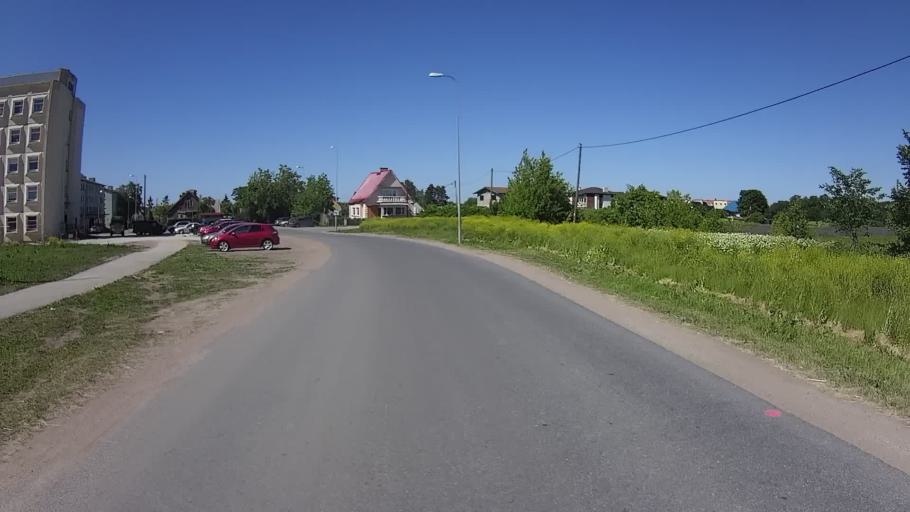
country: EE
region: Ida-Virumaa
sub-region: Kohtla-Jaerve linn
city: Kohtla-Jarve
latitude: 59.4045
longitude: 27.2982
